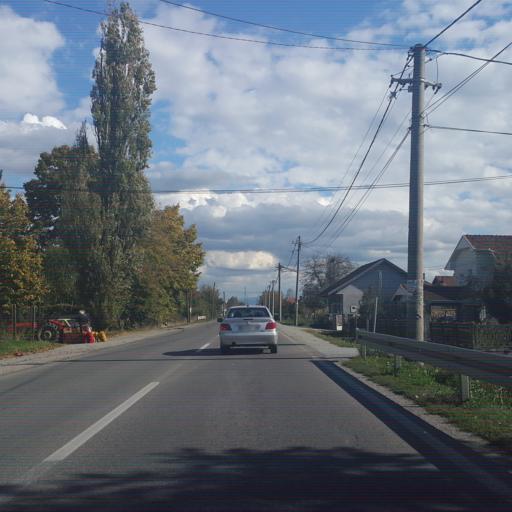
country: RS
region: Central Serbia
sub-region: Rasinski Okrug
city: Trstenik
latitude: 43.5996
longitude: 21.0521
